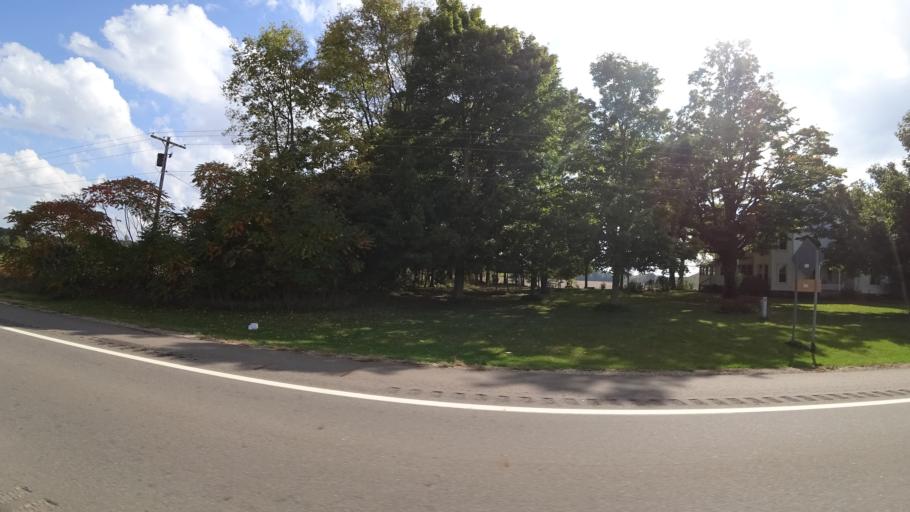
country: US
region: Michigan
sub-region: Branch County
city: Union City
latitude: 42.0677
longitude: -85.1779
